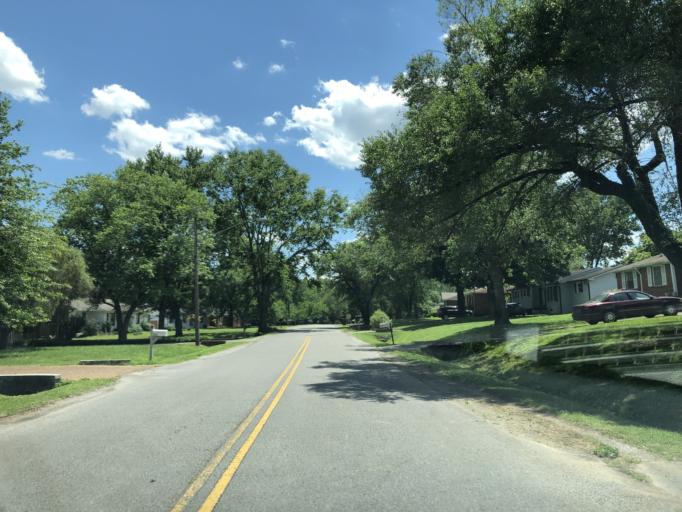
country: US
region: Tennessee
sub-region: Davidson County
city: Nashville
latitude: 36.1709
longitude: -86.7228
